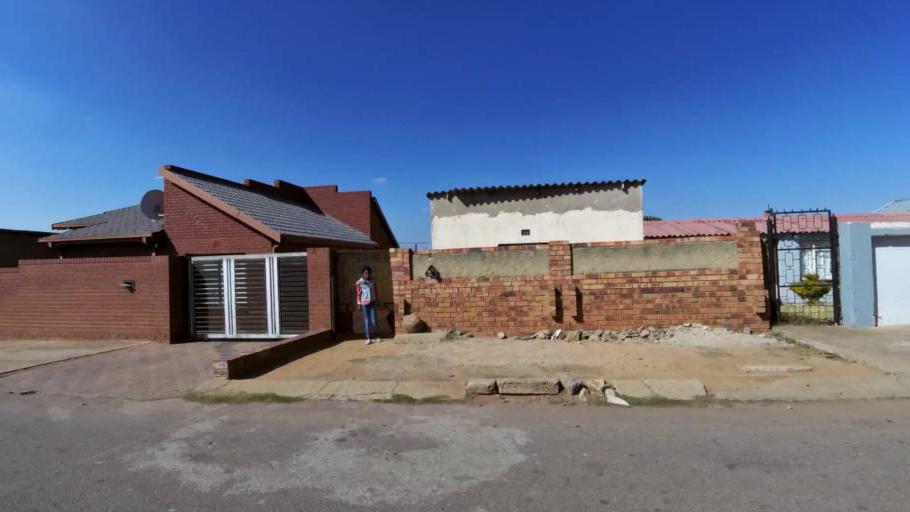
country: ZA
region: Gauteng
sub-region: City of Johannesburg Metropolitan Municipality
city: Soweto
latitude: -26.2338
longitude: 27.8838
